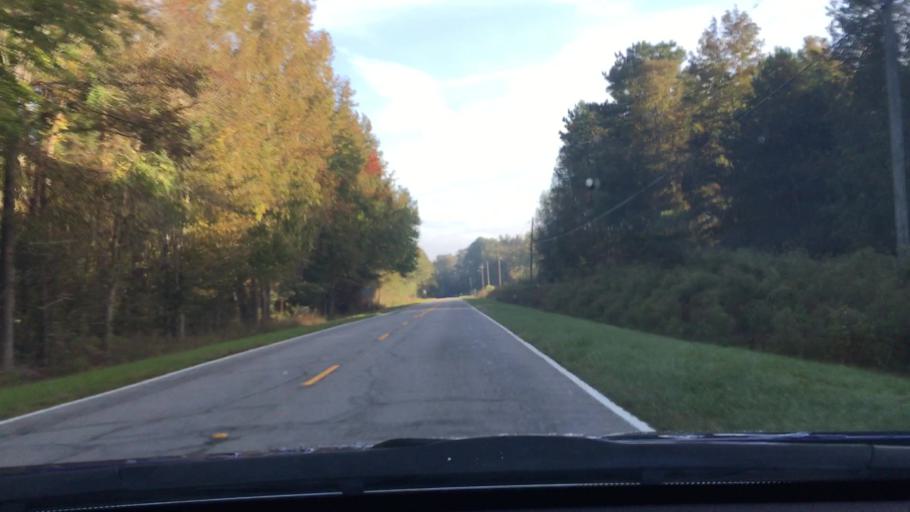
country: US
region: South Carolina
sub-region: Sumter County
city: East Sumter
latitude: 33.9581
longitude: -80.3049
